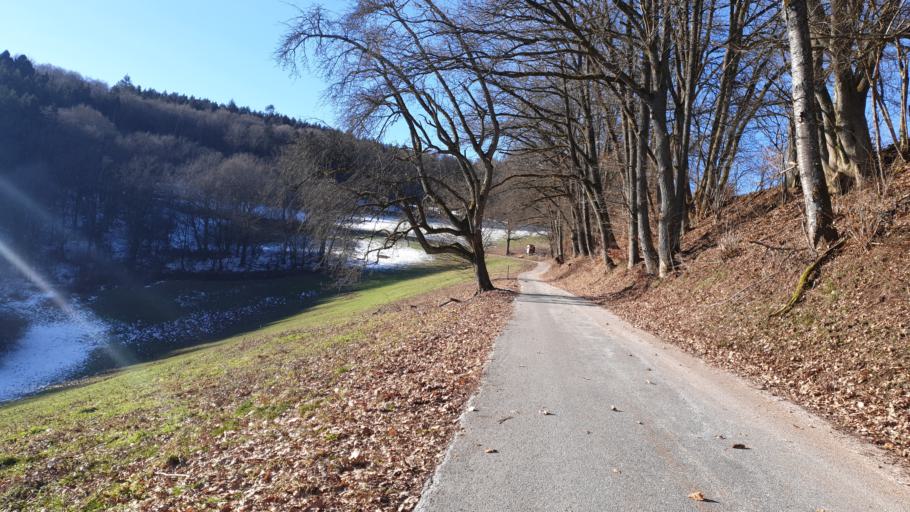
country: DE
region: Hesse
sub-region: Regierungsbezirk Darmstadt
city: Beerfelden
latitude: 49.5282
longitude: 8.9593
